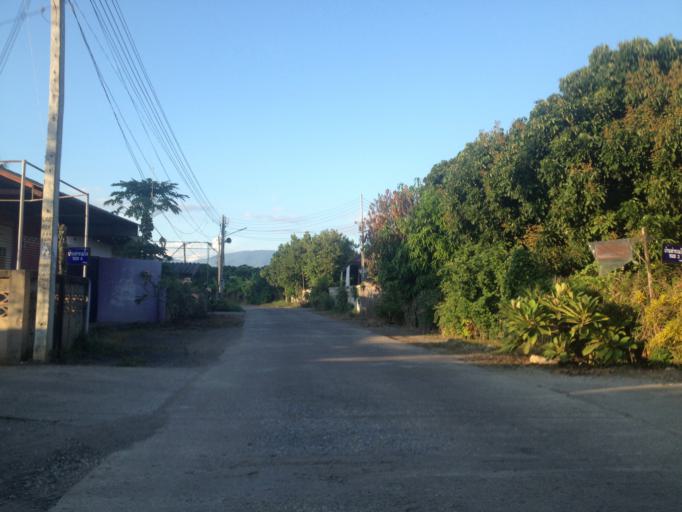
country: TH
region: Chiang Mai
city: San Pa Tong
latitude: 18.6584
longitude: 98.8877
